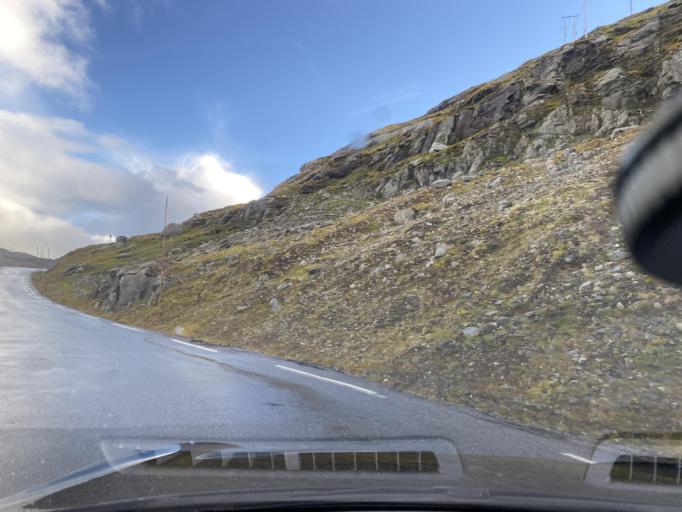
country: NO
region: Sogn og Fjordane
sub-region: Ardal
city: Farnes
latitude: 61.5748
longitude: 8.0307
